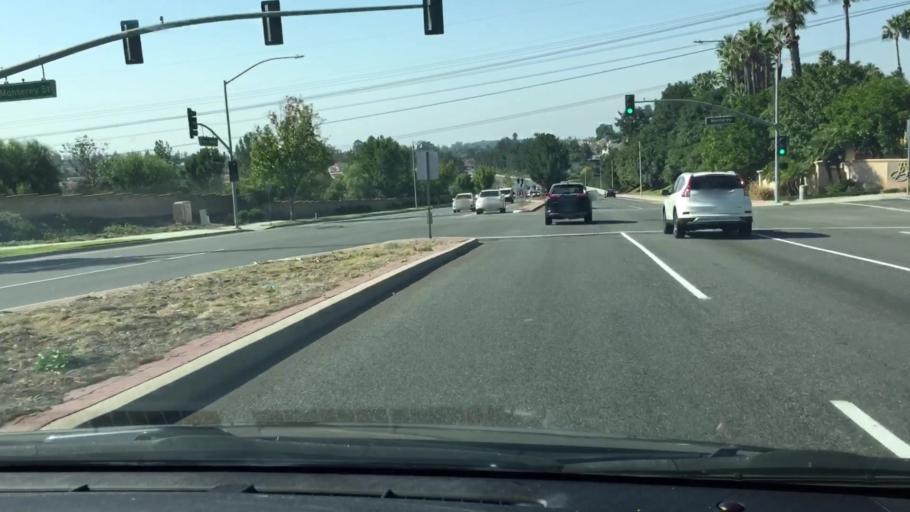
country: US
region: California
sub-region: Orange County
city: Portola Hills
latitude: 33.6502
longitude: -117.6340
